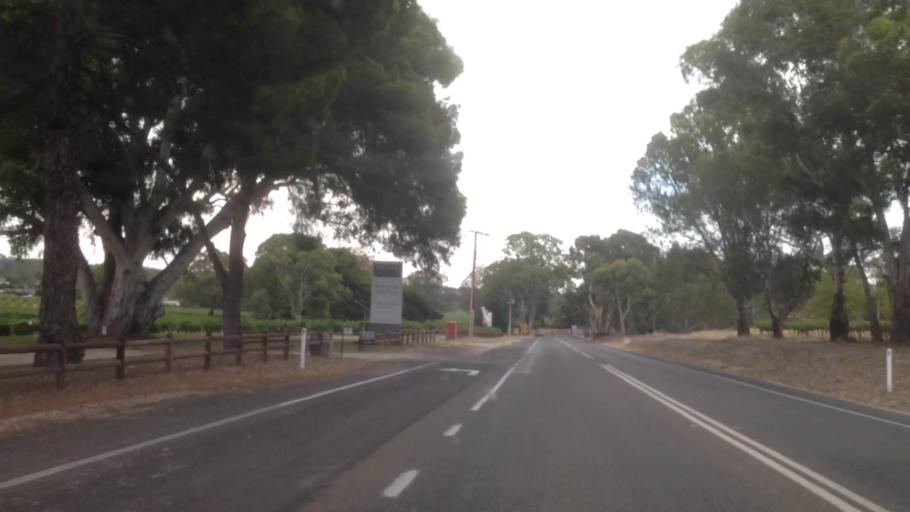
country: AU
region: South Australia
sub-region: Barossa
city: Lyndoch
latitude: -34.5993
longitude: 138.9026
